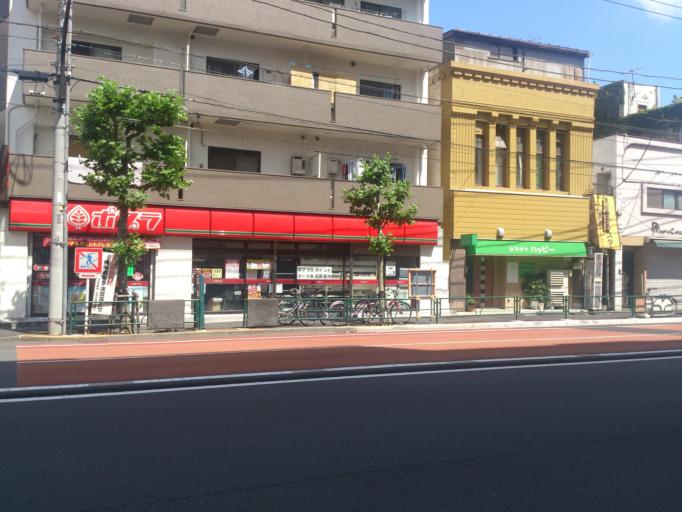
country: JP
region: Saitama
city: Soka
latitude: 35.7266
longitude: 139.8006
